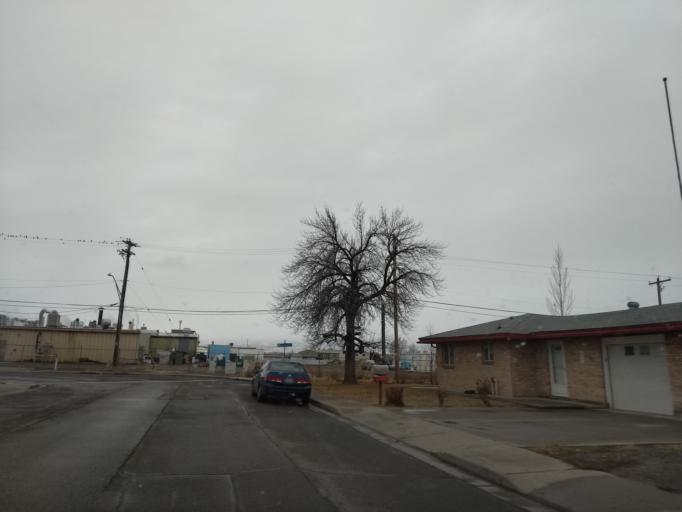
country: US
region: Colorado
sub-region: Mesa County
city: Grand Junction
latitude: 39.0741
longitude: -108.5254
